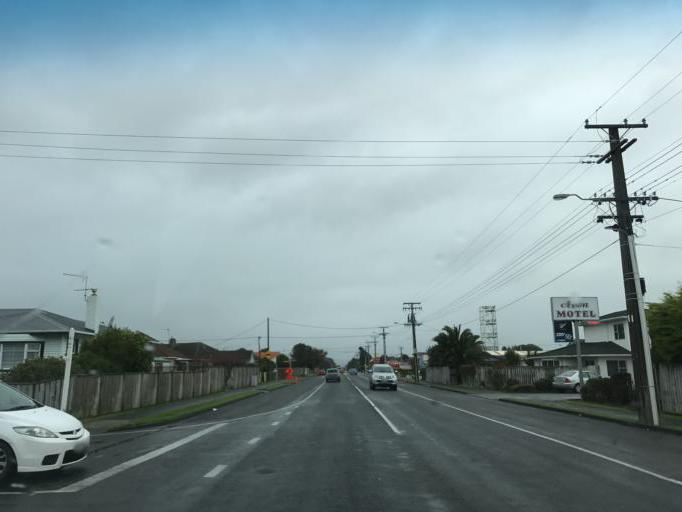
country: NZ
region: Taranaki
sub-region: South Taranaki District
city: Hawera
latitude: -39.5944
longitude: 174.2830
